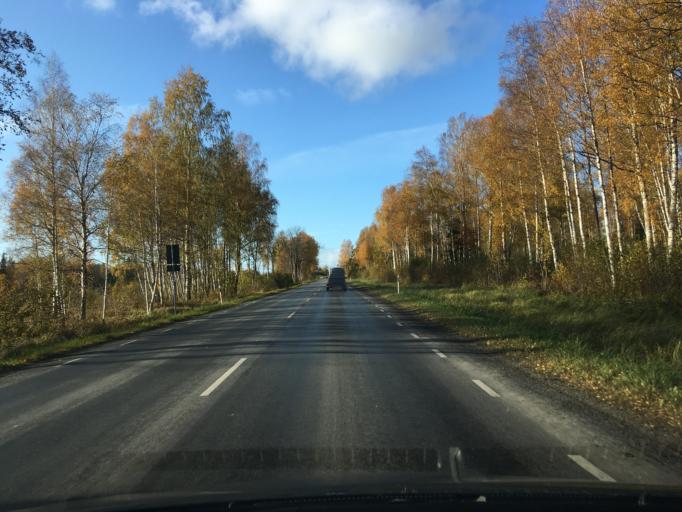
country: EE
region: Laeaene
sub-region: Lihula vald
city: Lihula
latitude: 58.5405
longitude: 24.0096
